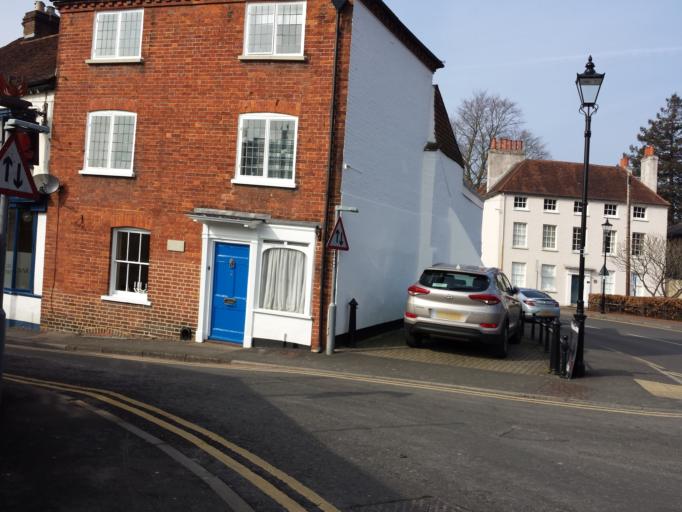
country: GB
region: England
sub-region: Surrey
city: Godalming
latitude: 51.1853
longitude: -0.6167
